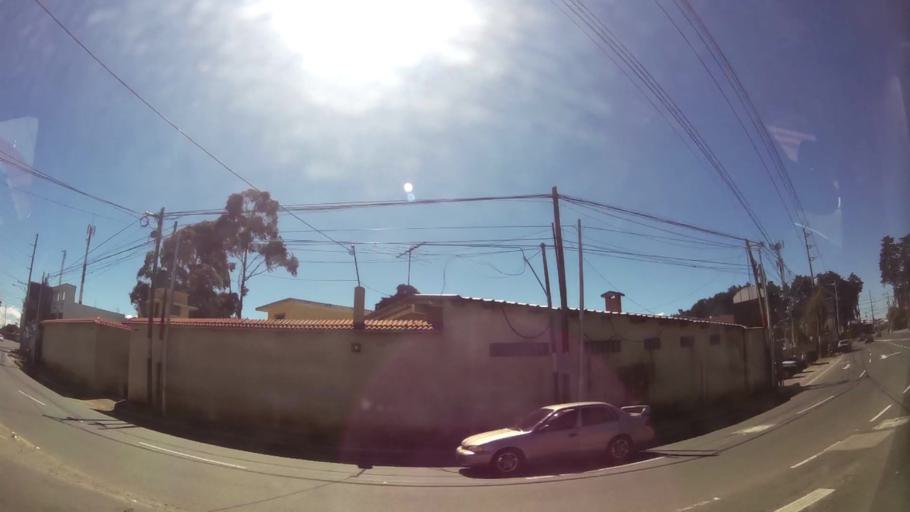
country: GT
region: Guatemala
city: San Jose Pinula
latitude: 14.5447
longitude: -90.4434
